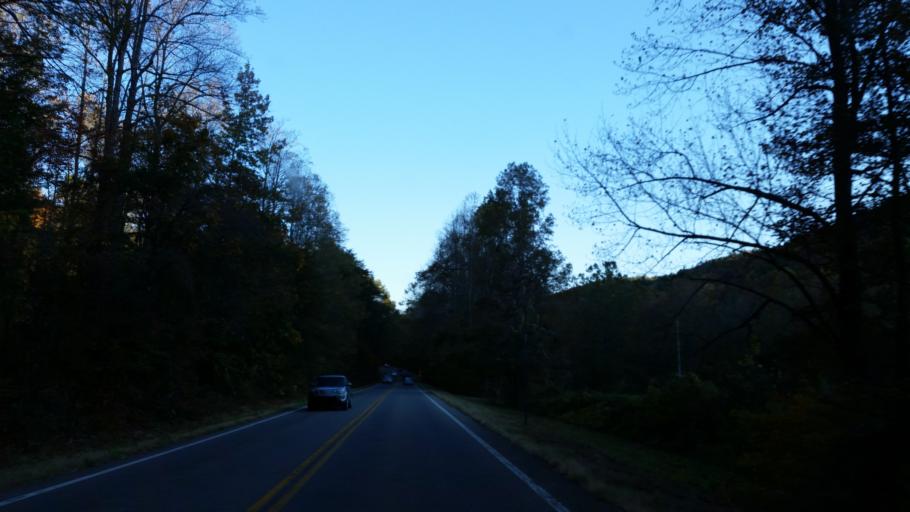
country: US
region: Georgia
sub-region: Pickens County
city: Jasper
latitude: 34.5567
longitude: -84.2960
